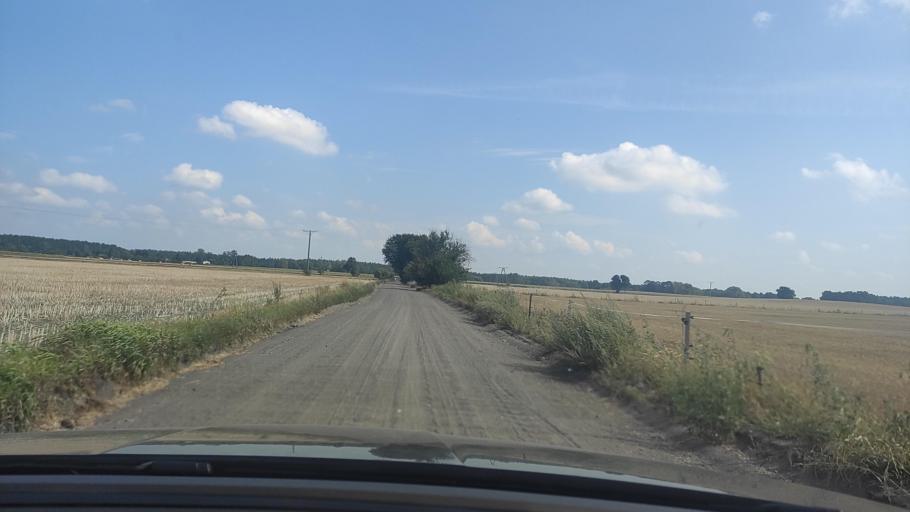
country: PL
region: Greater Poland Voivodeship
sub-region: Powiat poznanski
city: Kostrzyn
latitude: 52.4859
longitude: 17.1941
